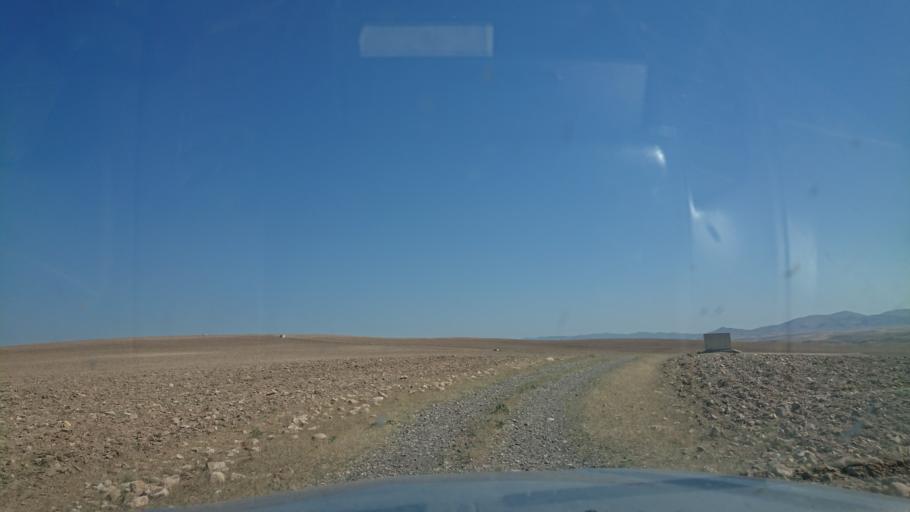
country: TR
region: Aksaray
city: Sariyahsi
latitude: 39.0518
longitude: 33.8886
